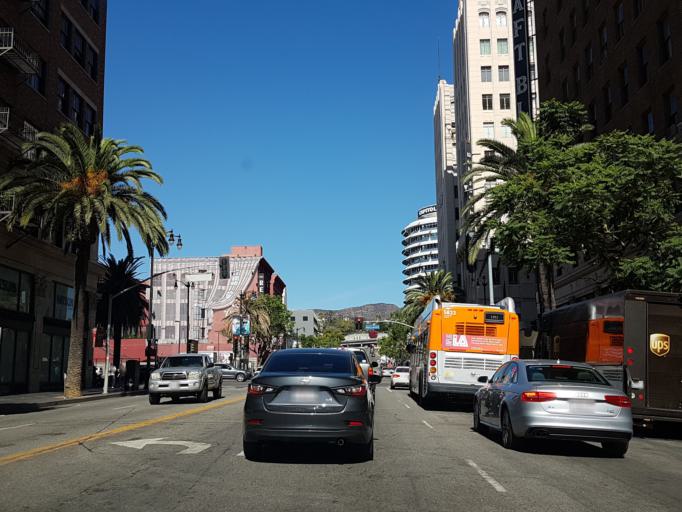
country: US
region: California
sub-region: Los Angeles County
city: Hollywood
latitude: 34.1010
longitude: -118.3267
